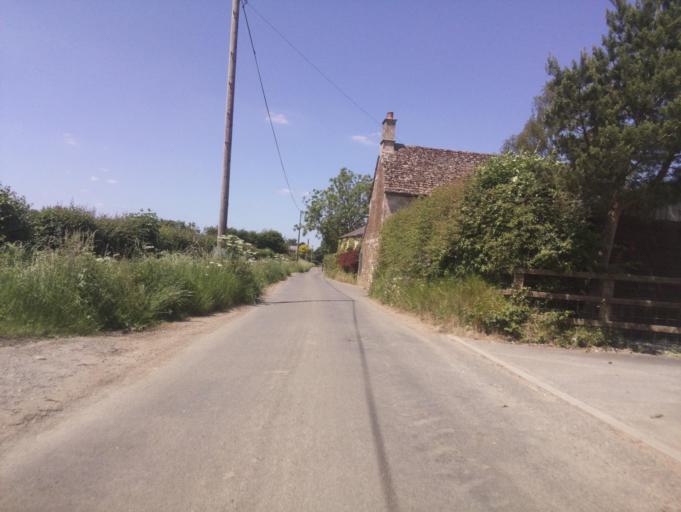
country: GB
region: England
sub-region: Wiltshire
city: Bremhill
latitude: 51.4651
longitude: -2.0733
